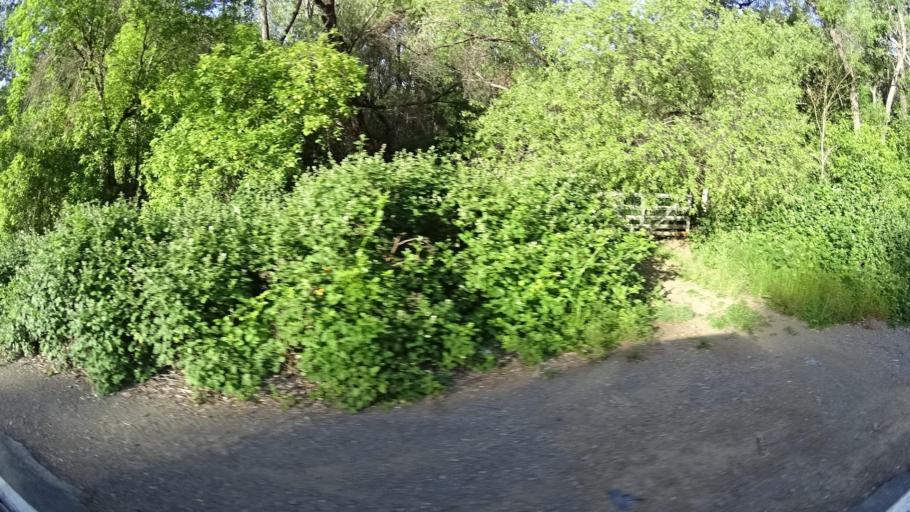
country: US
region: California
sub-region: Lake County
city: Upper Lake
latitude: 39.1574
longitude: -122.9931
